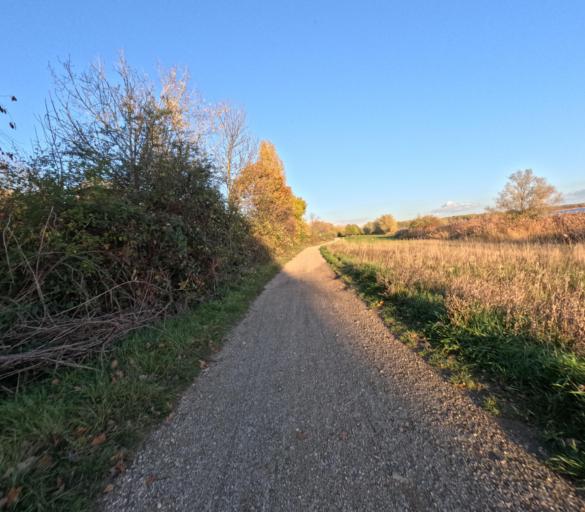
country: DE
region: Saxony-Anhalt
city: Rassnitz
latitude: 51.3866
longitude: 12.0924
